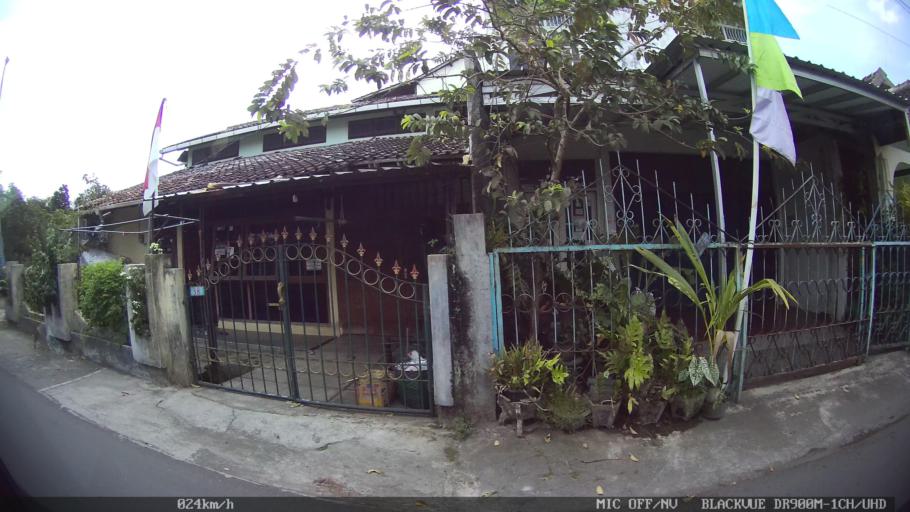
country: ID
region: Daerah Istimewa Yogyakarta
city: Kasihan
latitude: -7.8116
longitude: 110.3472
